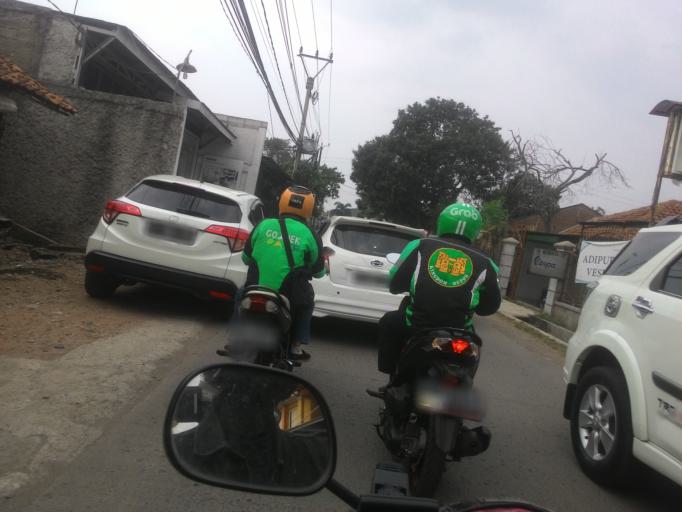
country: ID
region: West Java
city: Depok
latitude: -6.4243
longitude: 106.8376
